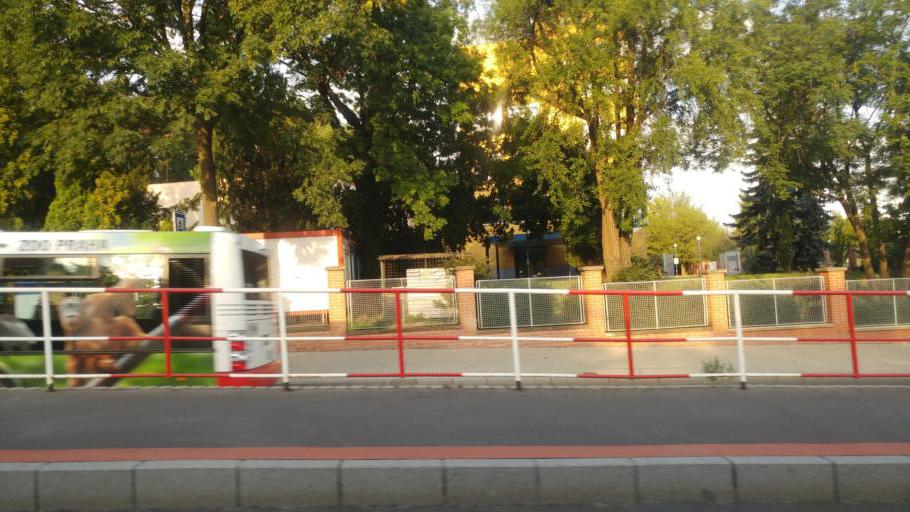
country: CZ
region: Praha
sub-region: Praha 8
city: Karlin
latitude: 50.1165
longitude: 14.4332
